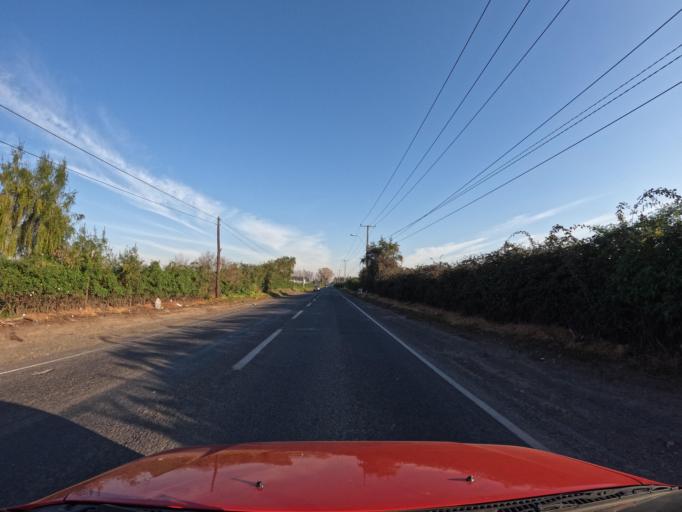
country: CL
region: Maule
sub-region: Provincia de Curico
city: Rauco
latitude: -34.9270
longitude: -71.2769
